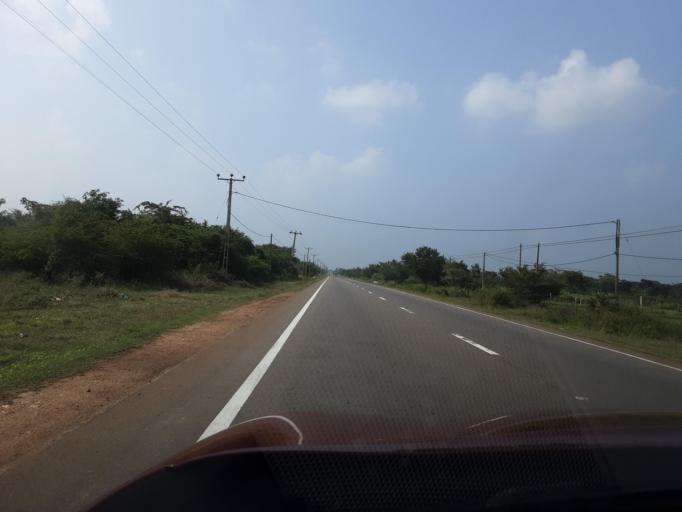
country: LK
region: Northern Province
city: Vavuniya
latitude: 9.0788
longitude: 80.4845
